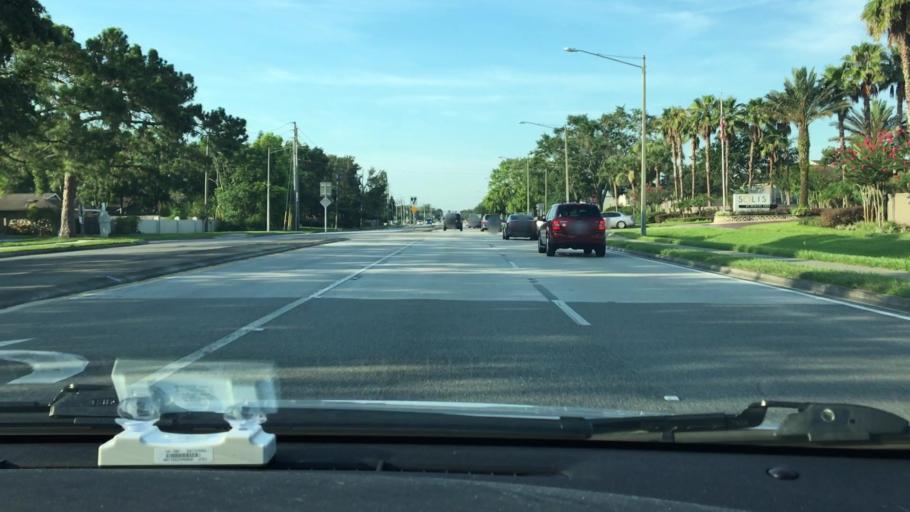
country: US
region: Florida
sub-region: Seminole County
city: Goldenrod
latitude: 28.6020
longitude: -81.2867
